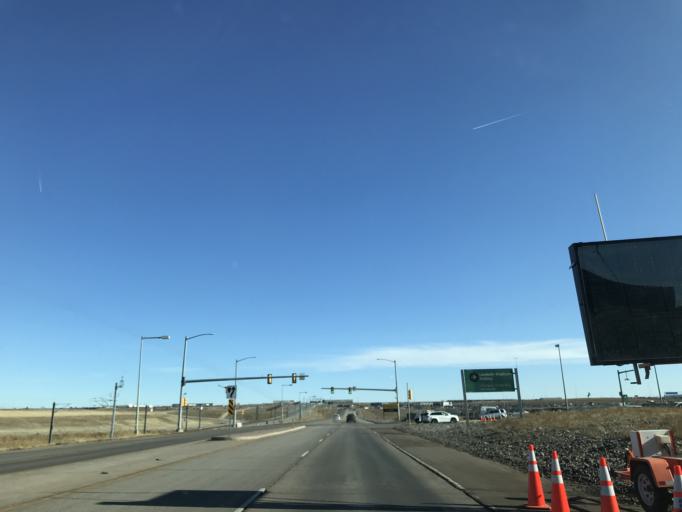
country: US
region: Colorado
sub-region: Weld County
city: Lochbuie
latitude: 39.8379
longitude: -104.6881
